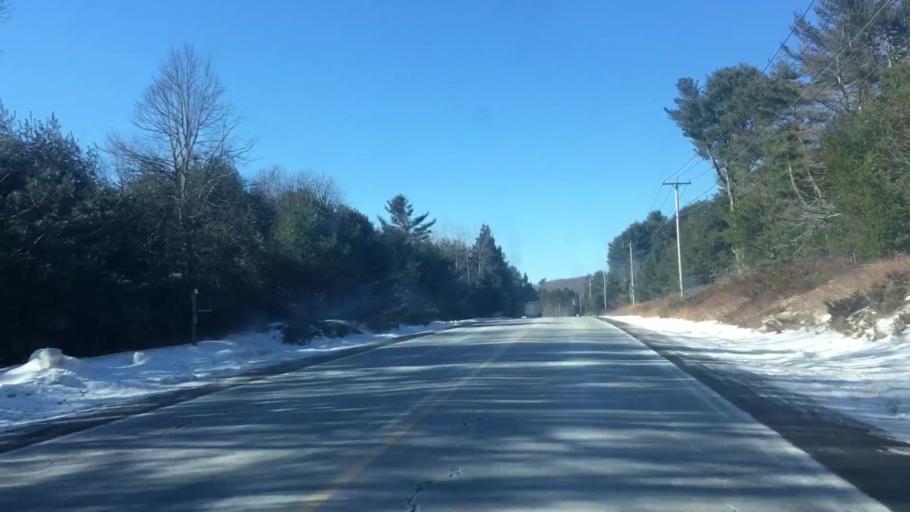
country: US
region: Maine
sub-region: Hancock County
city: Surry
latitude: 44.4959
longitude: -68.4826
